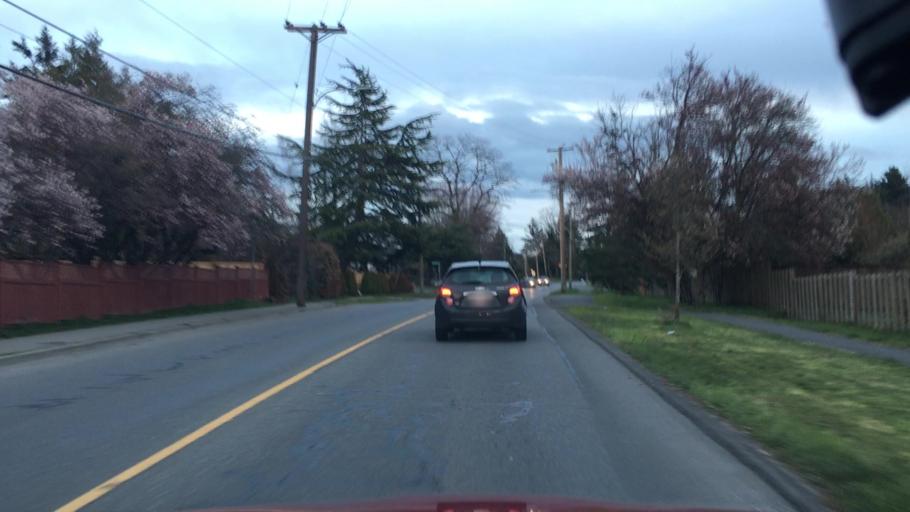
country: CA
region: British Columbia
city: Victoria
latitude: 48.4649
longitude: -123.3441
